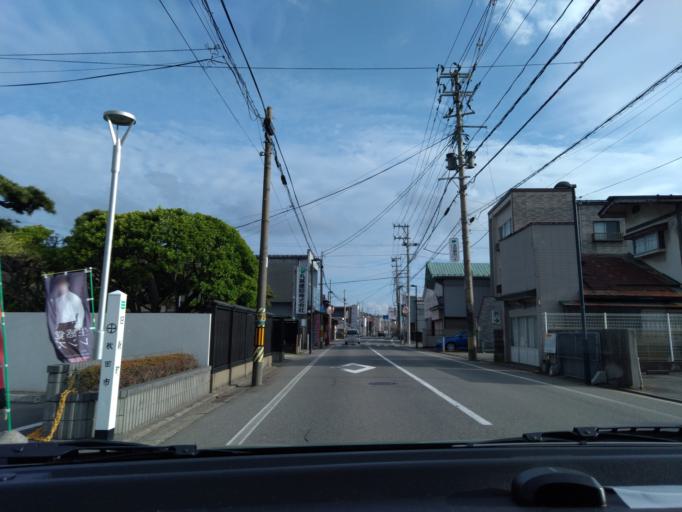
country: JP
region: Akita
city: Akita Shi
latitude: 39.7592
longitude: 140.0694
